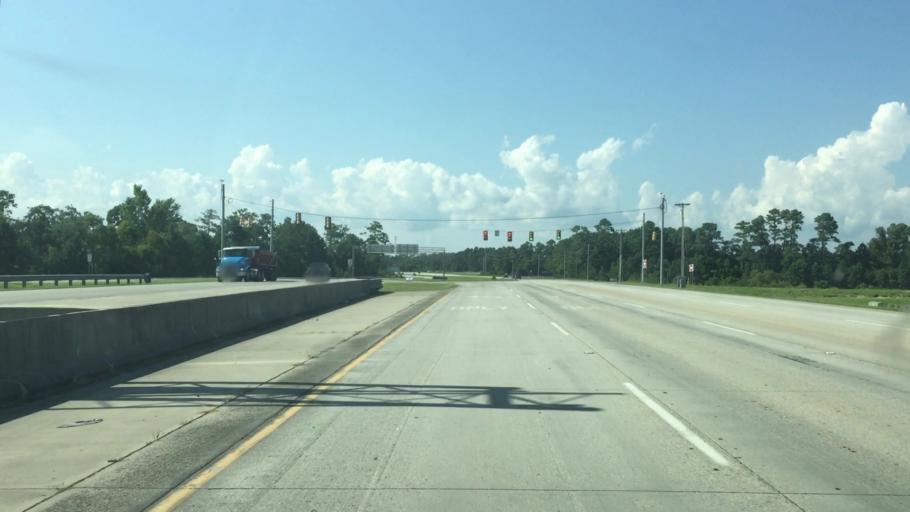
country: US
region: South Carolina
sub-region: Horry County
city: North Myrtle Beach
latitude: 33.8449
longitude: -78.7016
